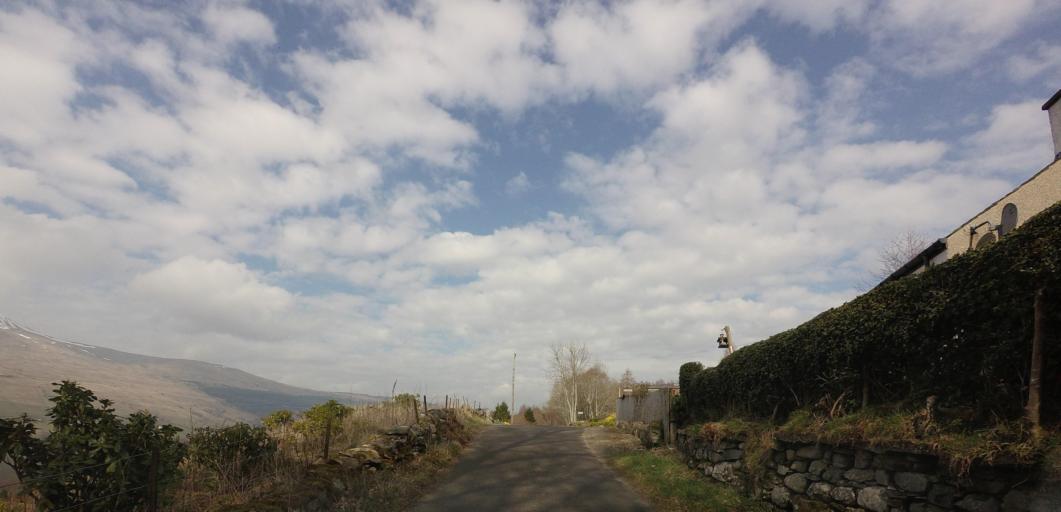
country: GB
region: Scotland
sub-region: Perth and Kinross
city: Comrie
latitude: 56.5311
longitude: -4.1087
